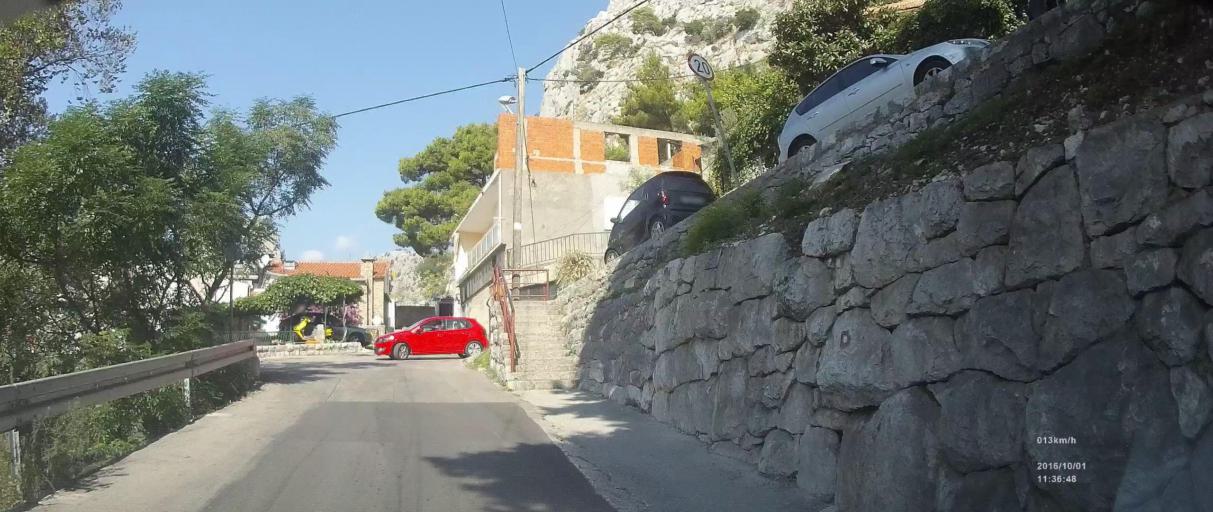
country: HR
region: Splitsko-Dalmatinska
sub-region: Grad Omis
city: Omis
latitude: 43.4430
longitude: 16.6950
